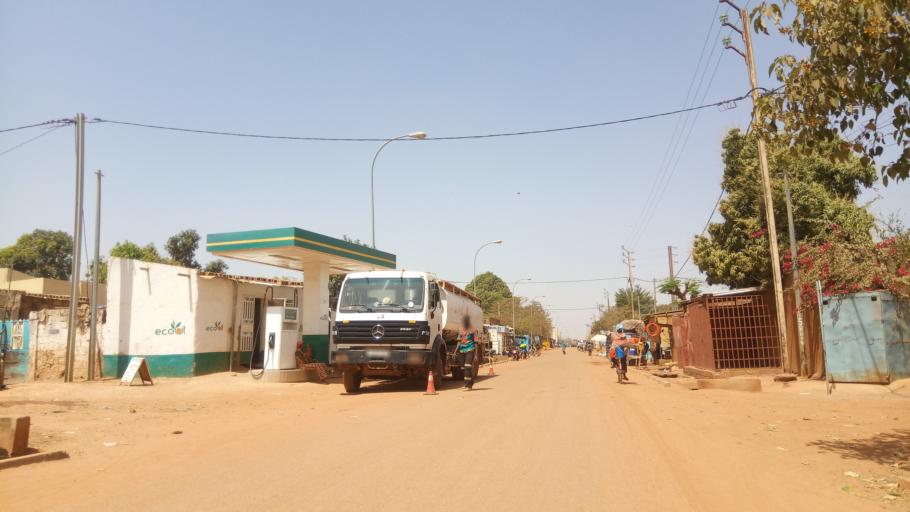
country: BF
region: Centre
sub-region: Kadiogo Province
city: Ouagadougou
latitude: 12.3923
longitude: -1.5628
